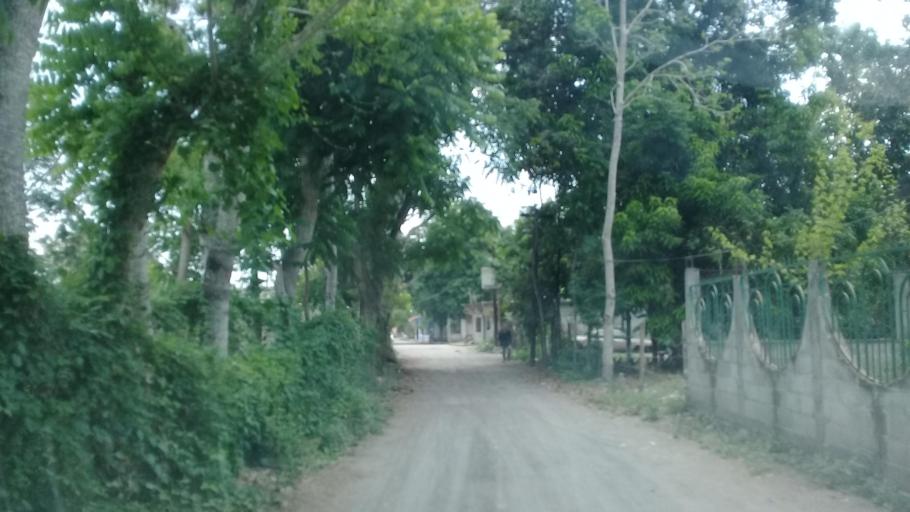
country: MX
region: Veracruz
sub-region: Emiliano Zapata
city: Plan del Rio
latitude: 19.4138
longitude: -96.6185
